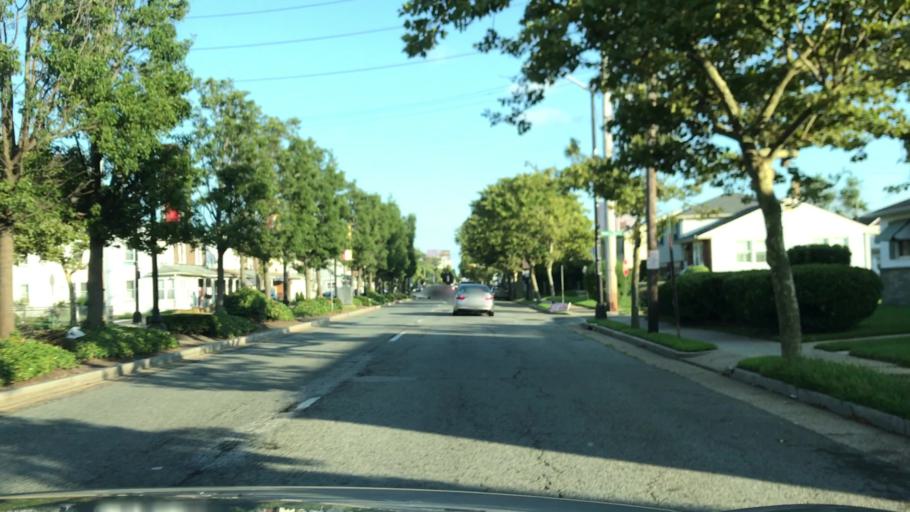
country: US
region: New Jersey
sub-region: Atlantic County
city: Atlantic City
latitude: 39.3678
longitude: -74.4368
